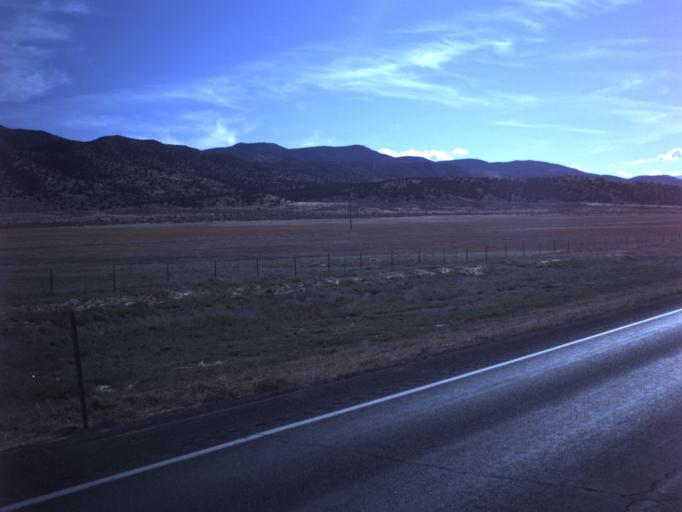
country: US
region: Utah
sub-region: Sanpete County
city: Gunnison
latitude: 39.3031
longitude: -111.8952
